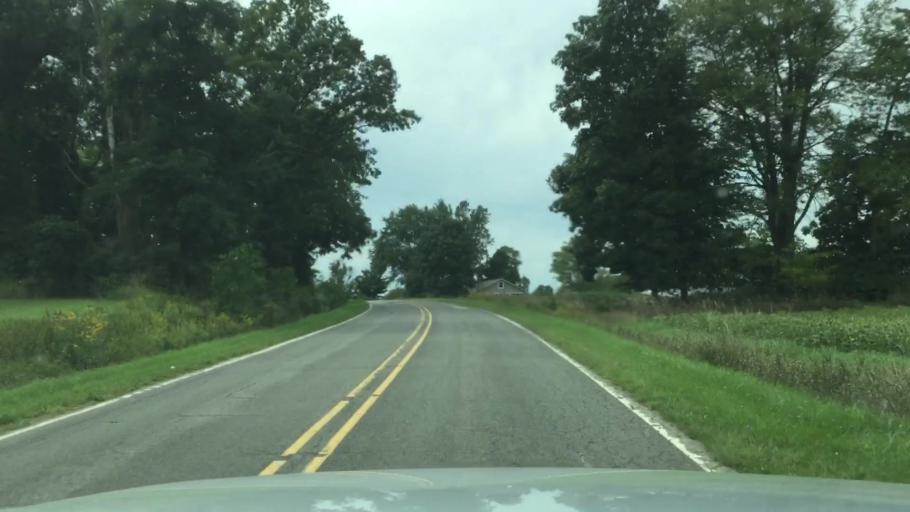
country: US
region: Michigan
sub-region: Shiawassee County
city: Corunna
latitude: 42.9361
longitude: -84.0994
